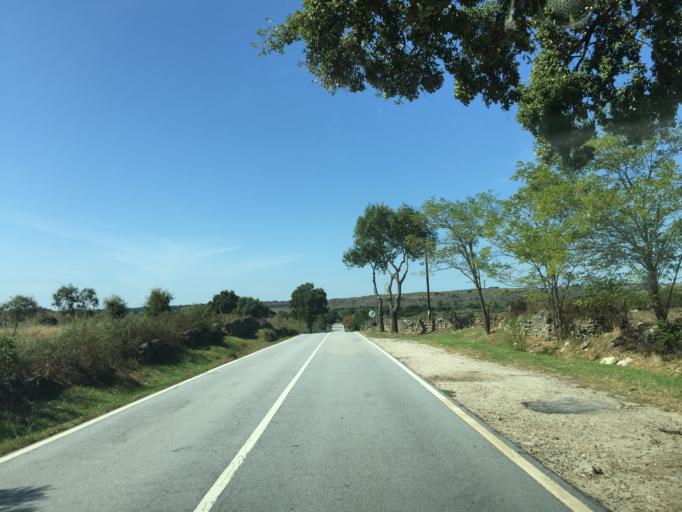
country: PT
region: Portalegre
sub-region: Castelo de Vide
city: Castelo de Vide
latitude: 39.4353
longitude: -7.5191
